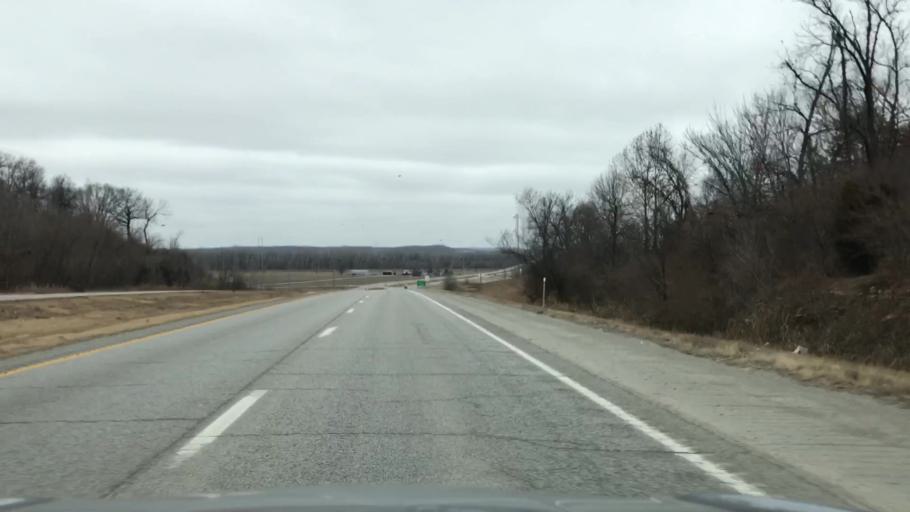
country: US
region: Missouri
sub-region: Jackson County
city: Independence
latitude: 39.1525
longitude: -94.3932
